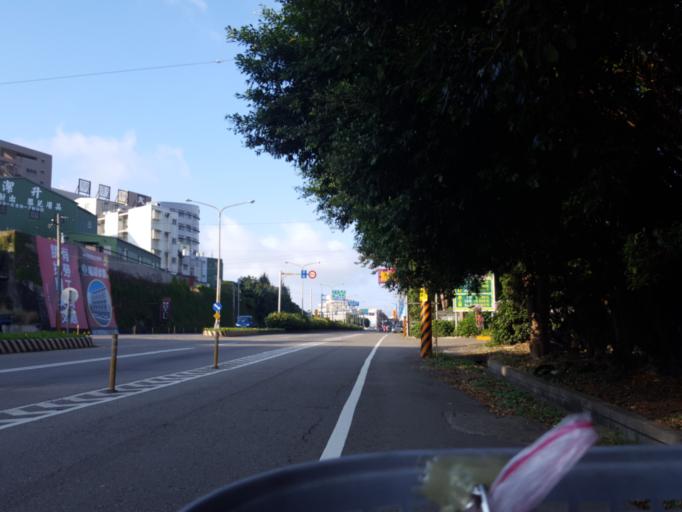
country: TW
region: Taiwan
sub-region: Hsinchu
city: Zhubei
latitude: 24.8611
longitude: 120.9915
